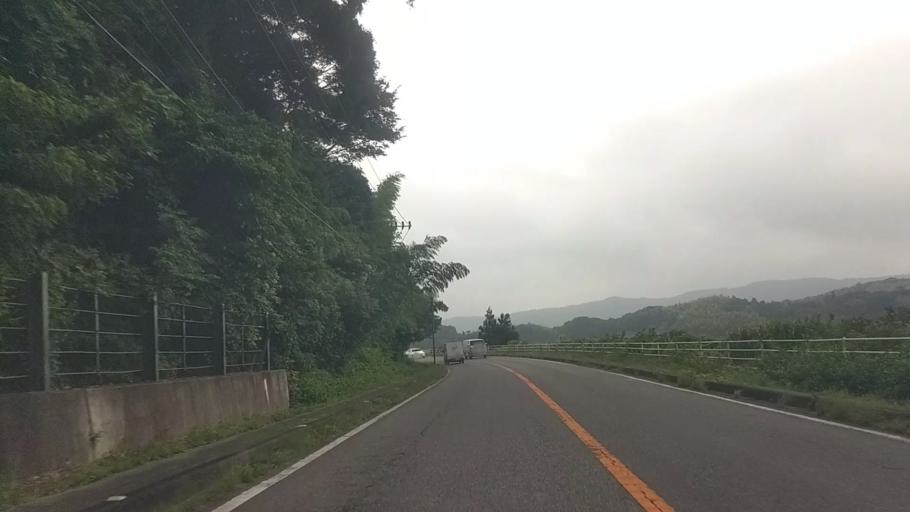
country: JP
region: Chiba
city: Kawaguchi
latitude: 35.1392
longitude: 140.0700
